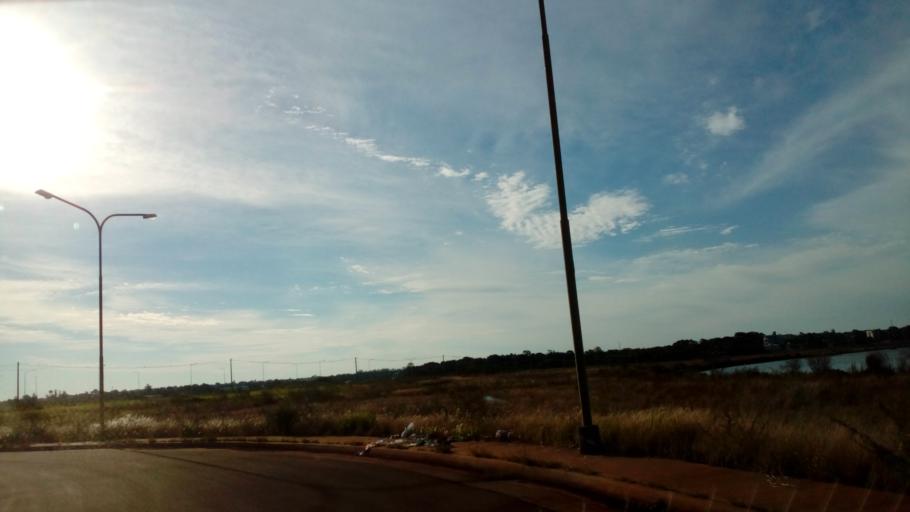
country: AR
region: Misiones
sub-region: Departamento de Capital
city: Posadas
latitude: -27.4122
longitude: -55.8857
